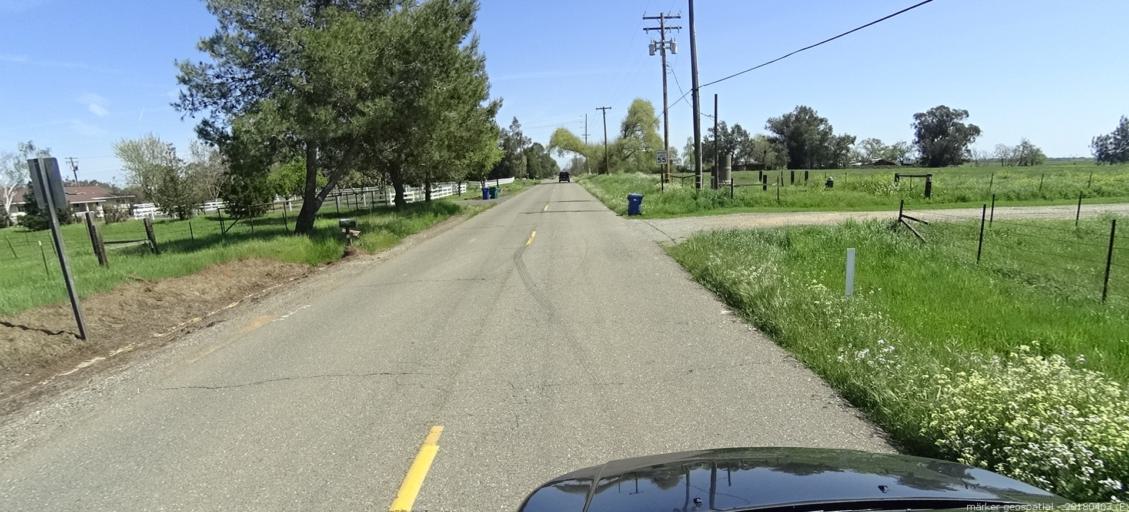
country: US
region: California
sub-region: Sacramento County
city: Wilton
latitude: 38.3798
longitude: -121.2764
